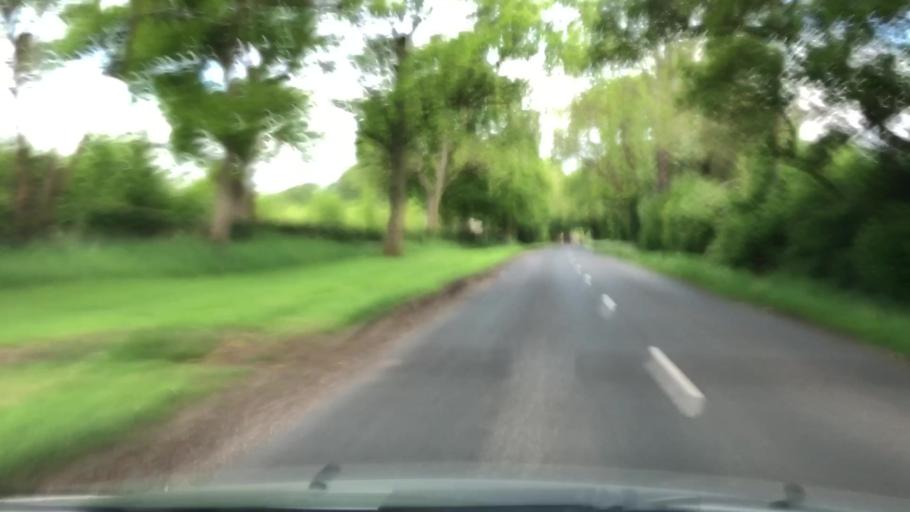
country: GB
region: England
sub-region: Hampshire
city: Alton
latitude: 51.1848
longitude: -0.9912
